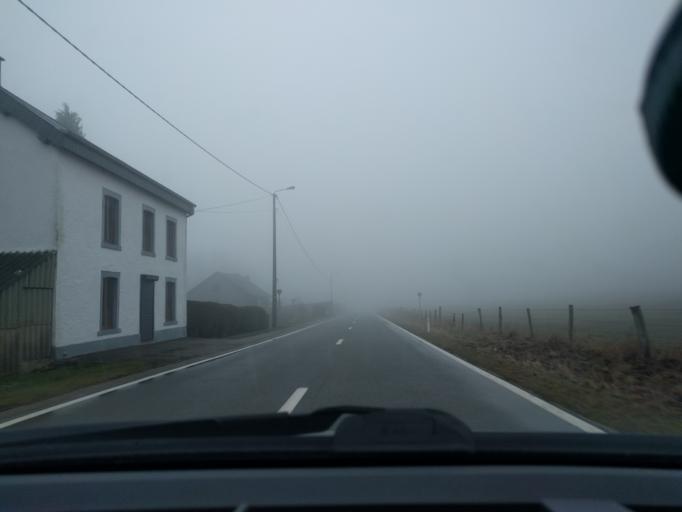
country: BE
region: Wallonia
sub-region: Province du Luxembourg
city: Gouvy
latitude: 50.1988
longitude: 5.9639
